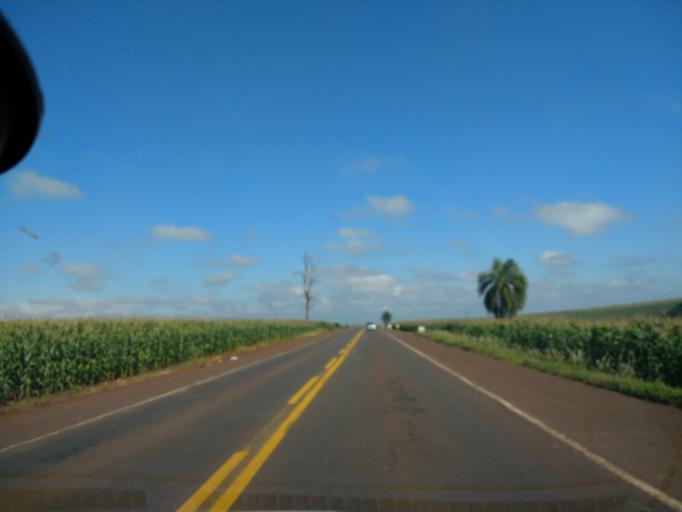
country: BR
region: Parana
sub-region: Paicandu
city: Paicandu
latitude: -23.5104
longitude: -52.1763
